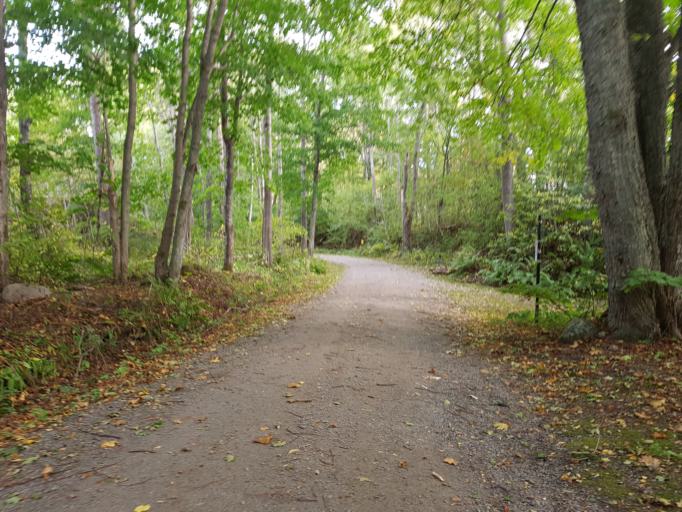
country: FI
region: Uusimaa
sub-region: Helsinki
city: Helsinki
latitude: 60.1354
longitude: 25.0023
